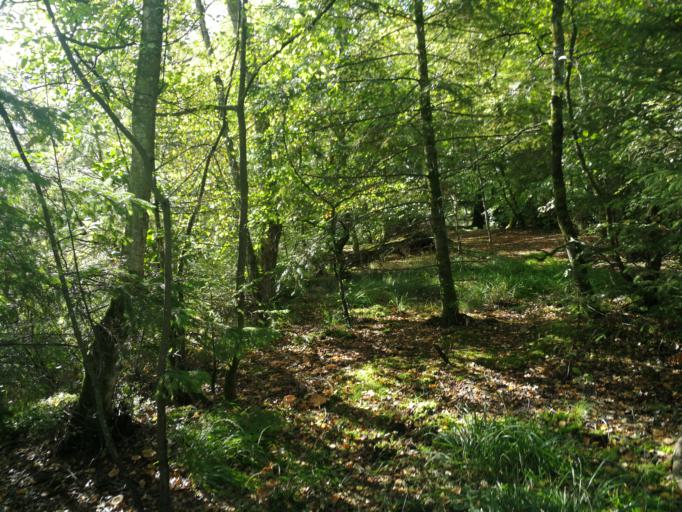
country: DK
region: Central Jutland
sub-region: Silkeborg Kommune
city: Virklund
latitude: 56.1455
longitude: 9.5764
